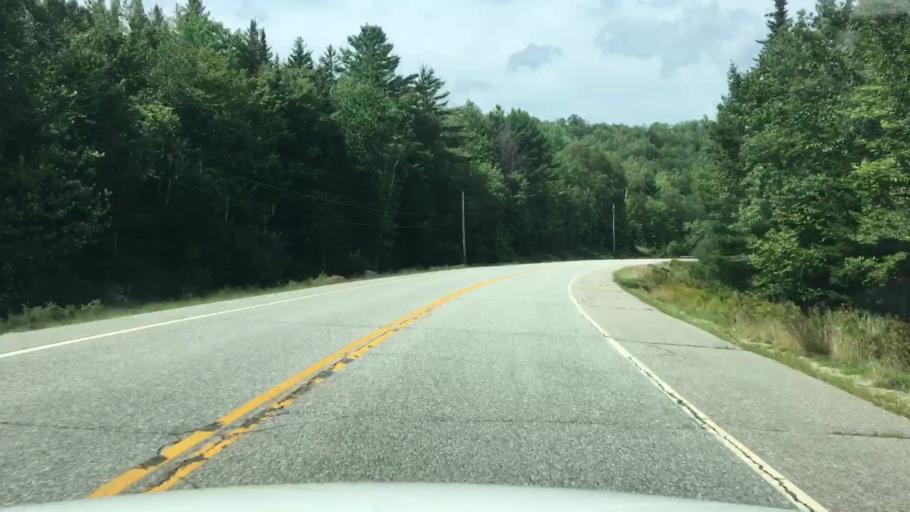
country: US
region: Maine
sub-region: Oxford County
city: Rumford
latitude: 44.5492
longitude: -70.7076
